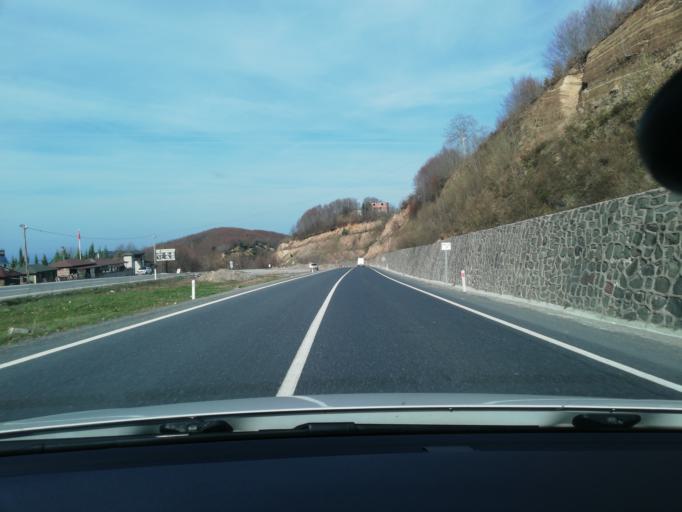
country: TR
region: Zonguldak
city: Kozlu
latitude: 41.3477
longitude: 31.6343
